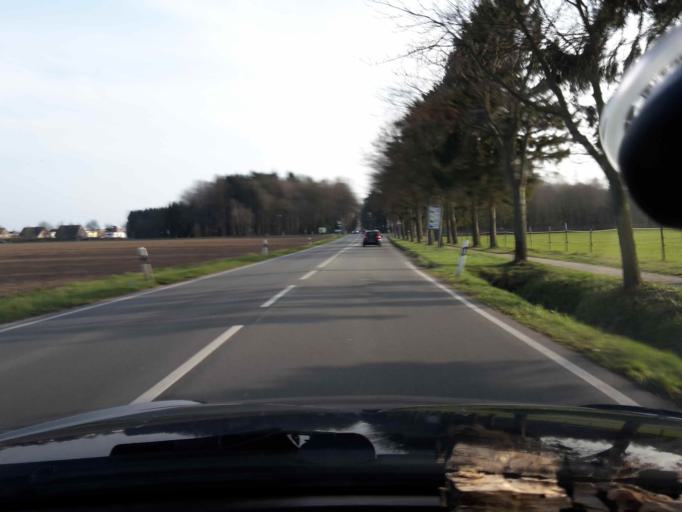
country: DE
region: Lower Saxony
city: Buchholz in der Nordheide
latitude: 53.3465
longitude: 9.8819
